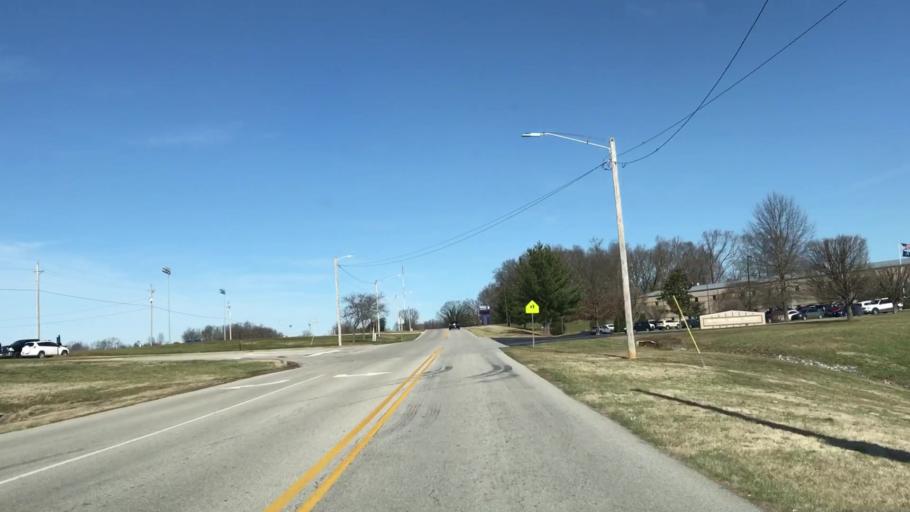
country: US
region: Kentucky
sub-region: Barren County
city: Glasgow
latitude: 37.0090
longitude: -85.8864
